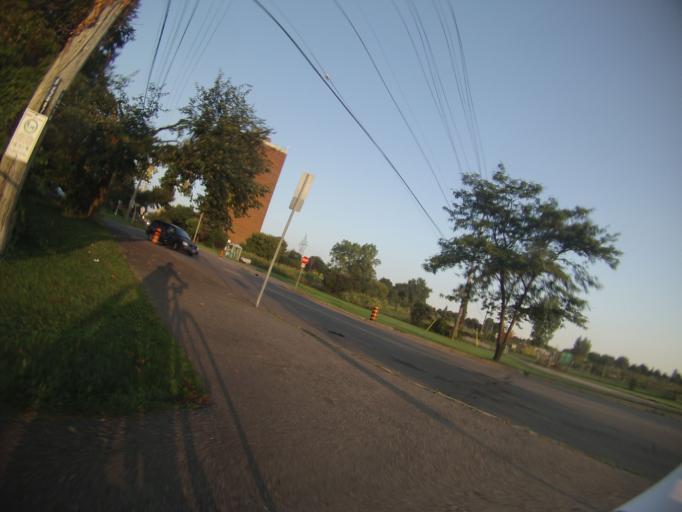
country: CA
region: Ontario
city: Ottawa
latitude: 45.3883
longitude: -75.6376
